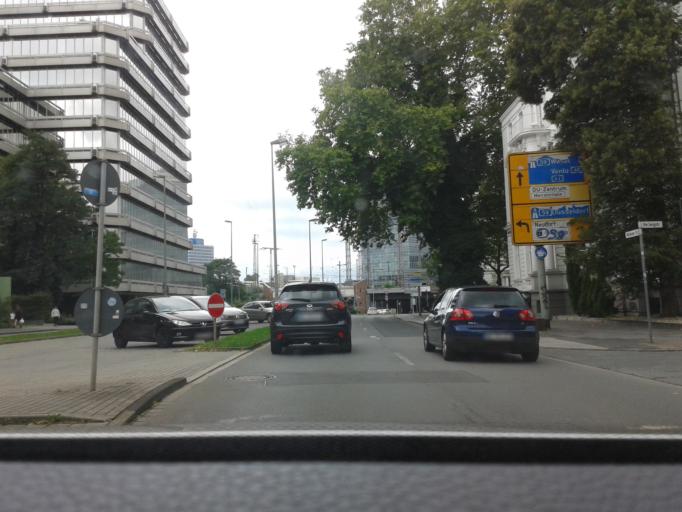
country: DE
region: North Rhine-Westphalia
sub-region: Regierungsbezirk Dusseldorf
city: Duisburg
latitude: 51.4323
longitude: 6.7810
